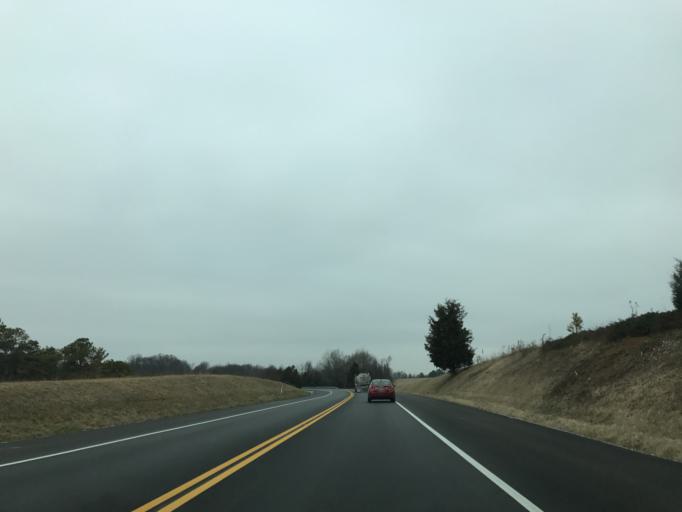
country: US
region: Maryland
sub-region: Carroll County
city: New Windsor
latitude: 39.6154
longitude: -77.0820
